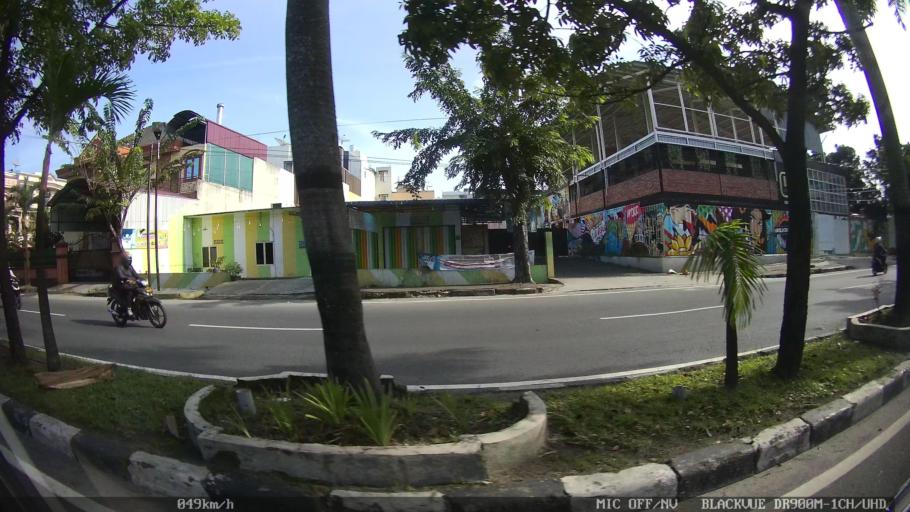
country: ID
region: North Sumatra
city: Medan
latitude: 3.6078
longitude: 98.6580
